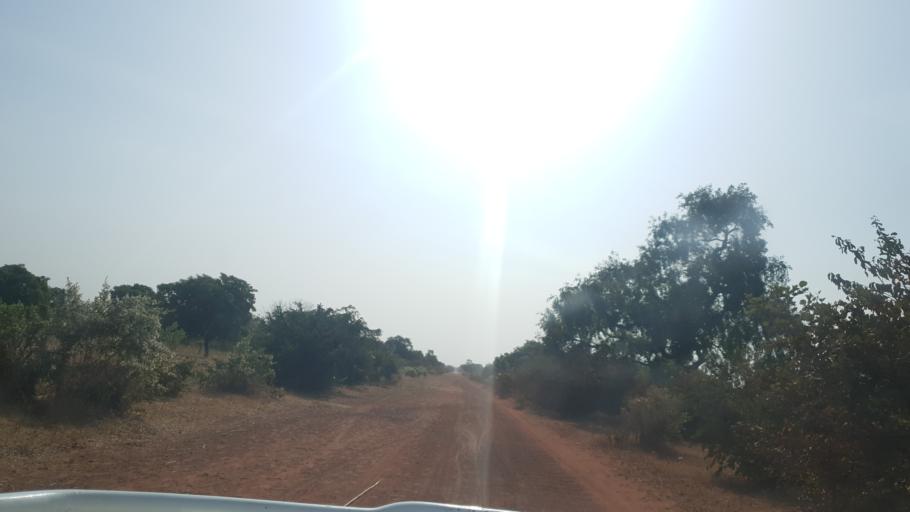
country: ML
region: Koulikoro
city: Dioila
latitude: 12.7028
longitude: -6.7658
